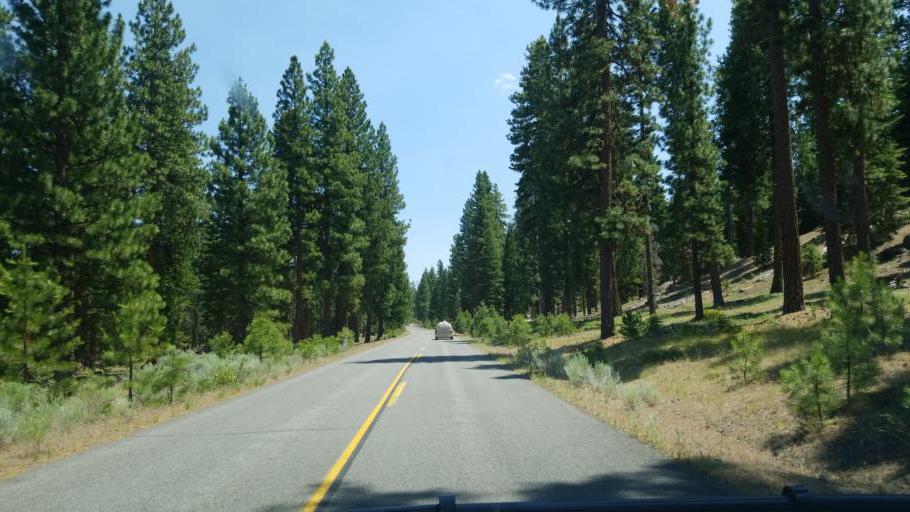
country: US
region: California
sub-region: Lassen County
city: Susanville
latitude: 40.5552
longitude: -120.8254
